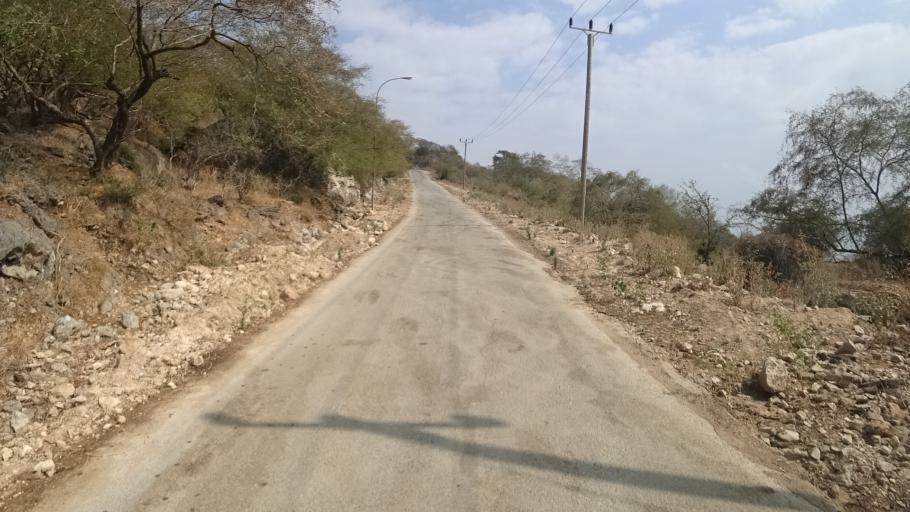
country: YE
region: Al Mahrah
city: Hawf
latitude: 16.7188
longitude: 53.2597
